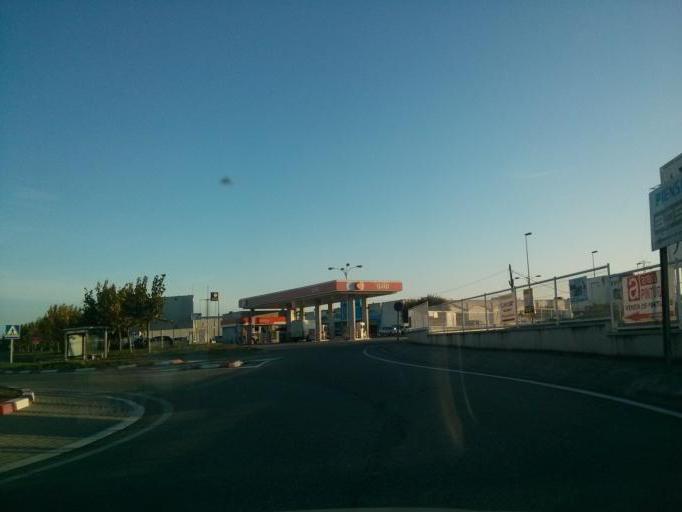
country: ES
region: Catalonia
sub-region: Provincia de Tarragona
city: Santa Oliva
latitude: 41.2357
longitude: 1.5437
